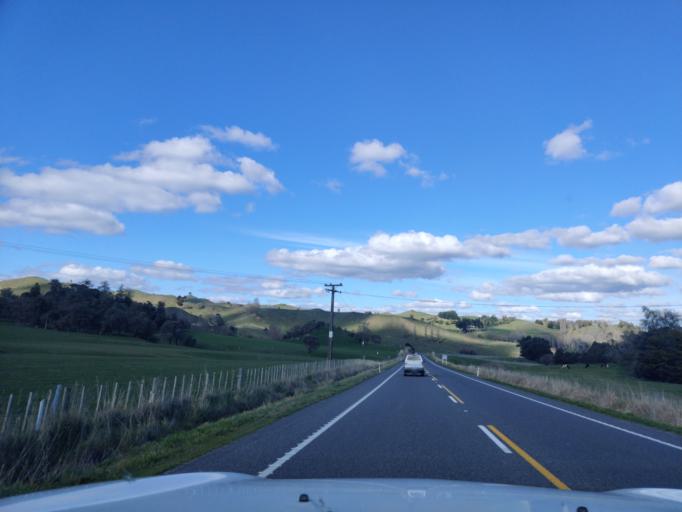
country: NZ
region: Manawatu-Wanganui
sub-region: Ruapehu District
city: Waiouru
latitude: -39.6315
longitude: 175.7633
